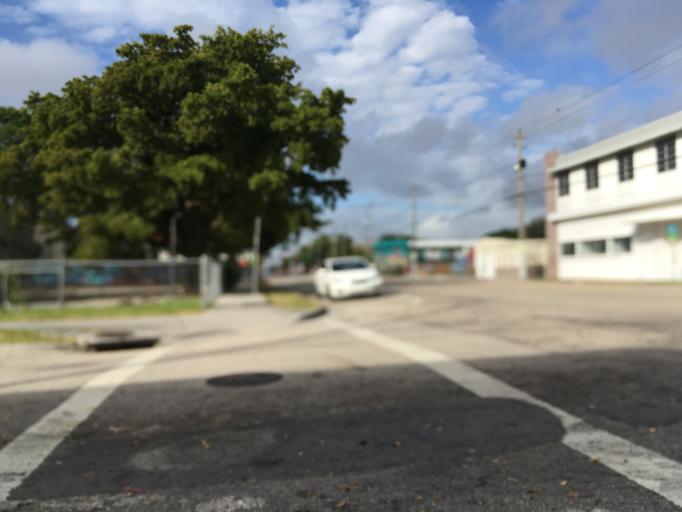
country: US
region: Florida
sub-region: Miami-Dade County
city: Allapattah
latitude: 25.8039
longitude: -80.1971
